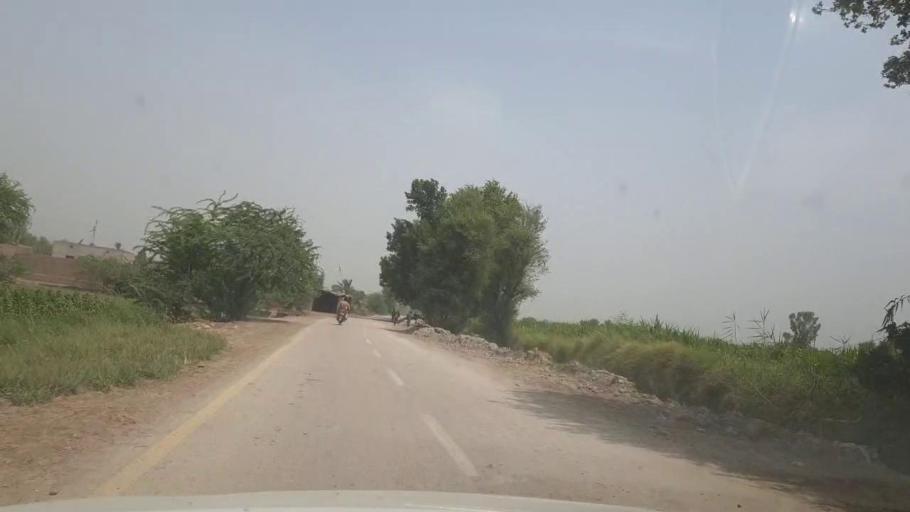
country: PK
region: Sindh
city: Kot Diji
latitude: 27.3818
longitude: 68.6546
